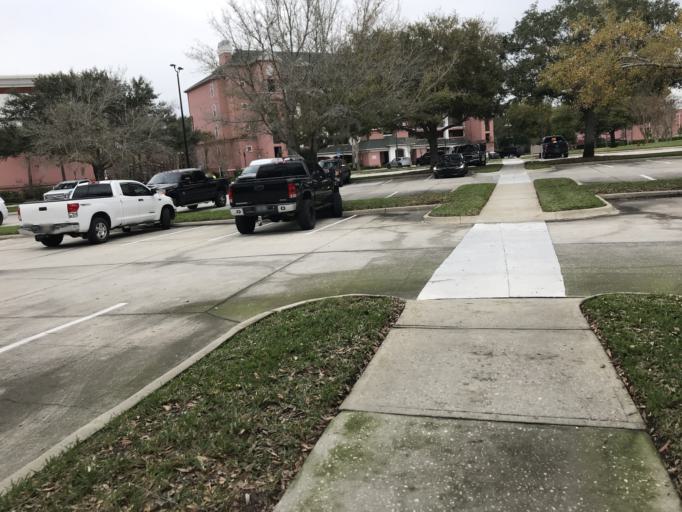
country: US
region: Florida
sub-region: Osceola County
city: Celebration
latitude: 28.3599
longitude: -81.4924
